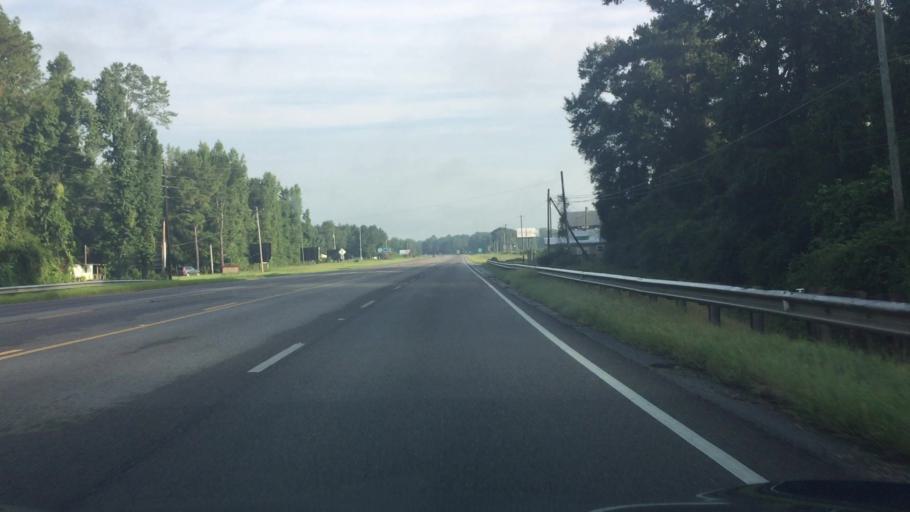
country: US
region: Alabama
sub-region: Covington County
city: Andalusia
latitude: 31.3382
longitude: -86.5218
